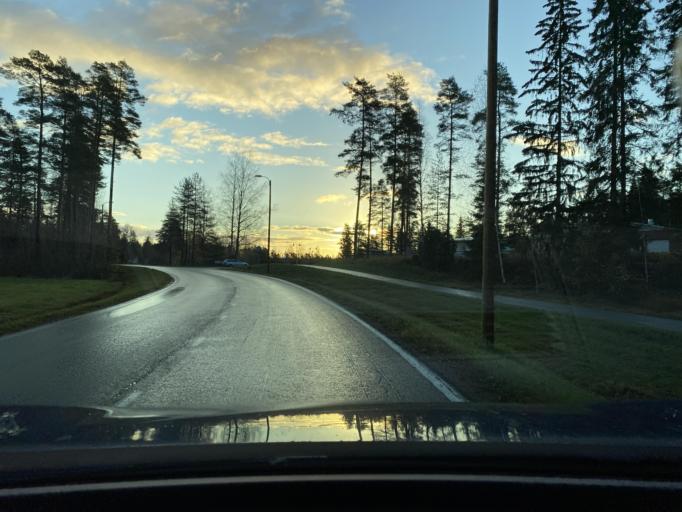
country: FI
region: Varsinais-Suomi
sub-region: Loimaa
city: Aura
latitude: 60.7228
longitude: 22.5906
